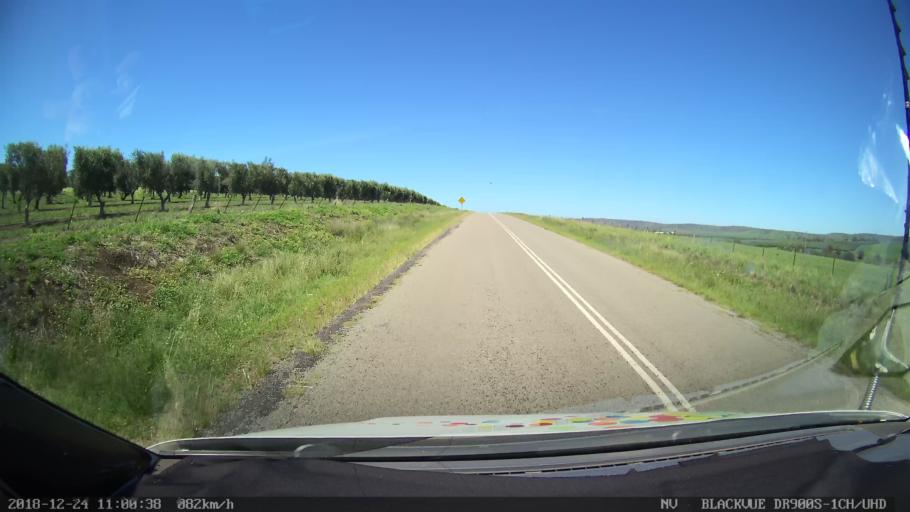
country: AU
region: New South Wales
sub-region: Upper Hunter Shire
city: Merriwa
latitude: -32.0696
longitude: 150.3927
